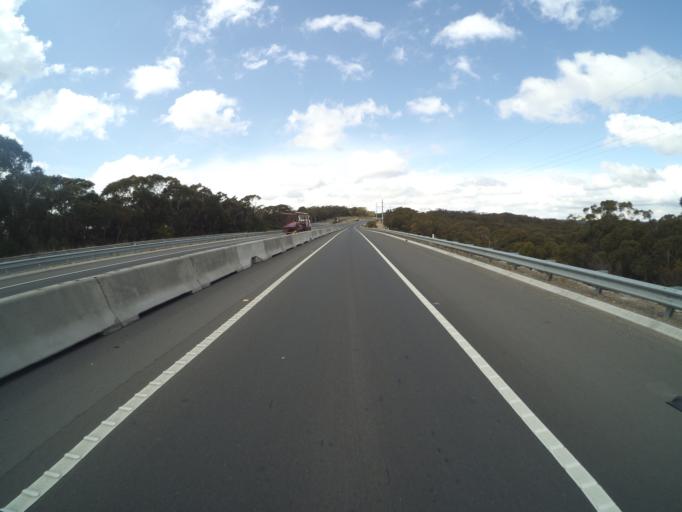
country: AU
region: New South Wales
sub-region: Wollongong
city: Mount Keira
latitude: -34.3547
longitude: 150.8085
